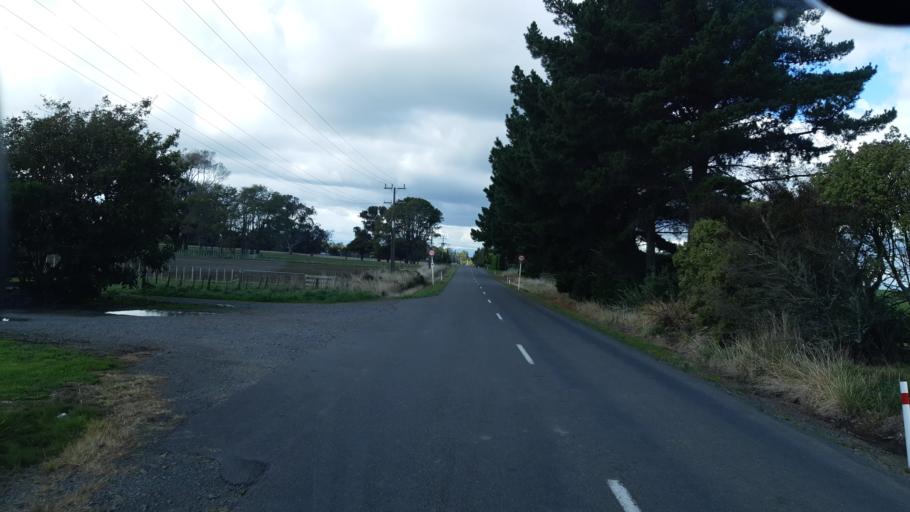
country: NZ
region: Manawatu-Wanganui
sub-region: Rangitikei District
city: Bulls
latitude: -40.0983
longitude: 175.3750
